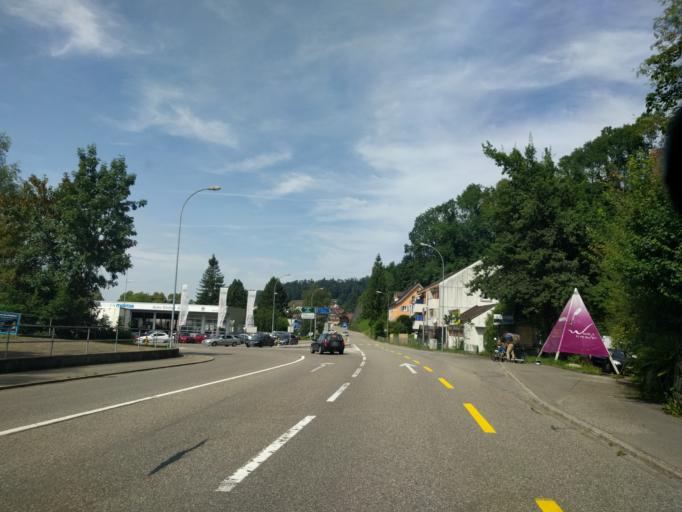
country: CH
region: Saint Gallen
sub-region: Wahlkreis Toggenburg
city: Lichtensteig
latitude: 47.3141
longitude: 9.0844
